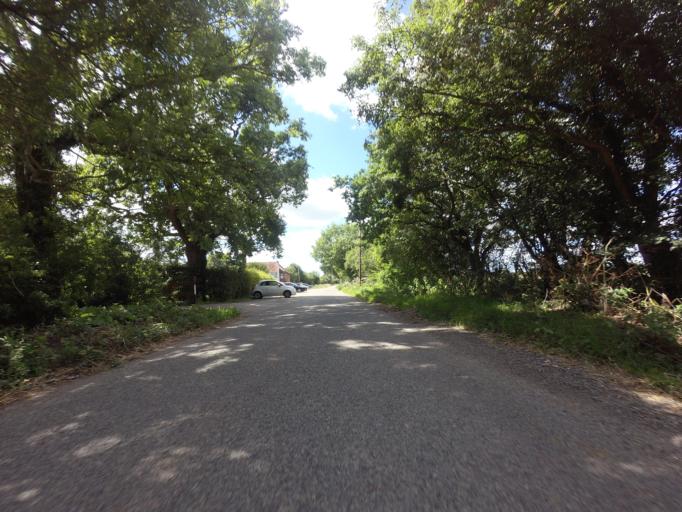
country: GB
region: England
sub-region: East Sussex
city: Hailsham
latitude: 50.8696
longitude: 0.1661
